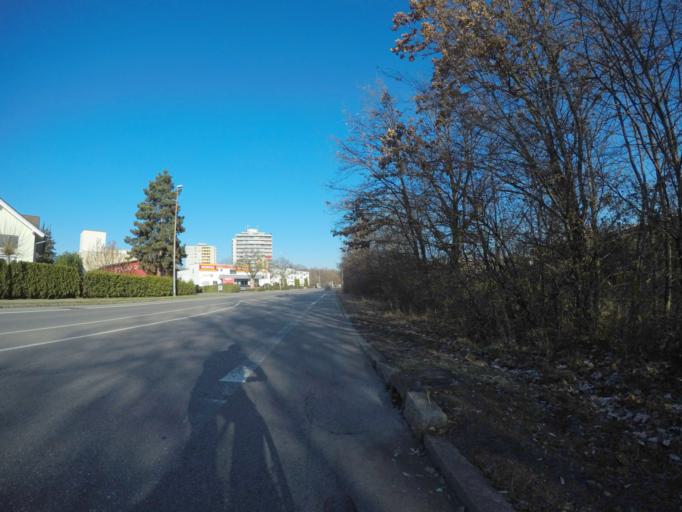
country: DE
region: Baden-Wuerttemberg
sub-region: Tuebingen Region
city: Reutlingen
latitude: 48.5090
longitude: 9.2170
